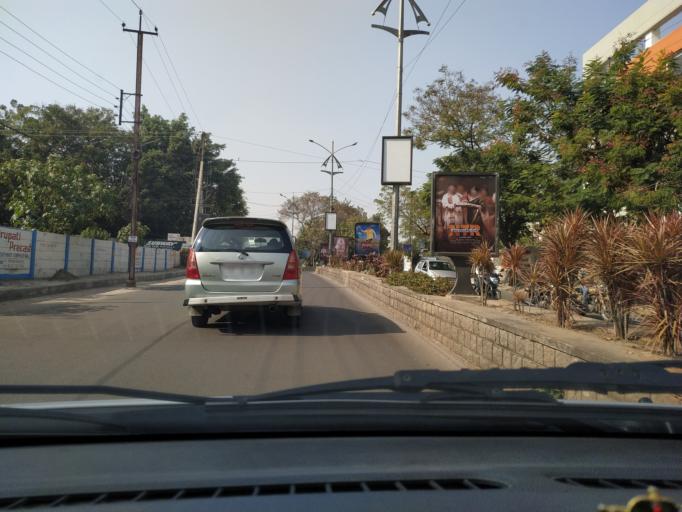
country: IN
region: Telangana
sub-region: Rangareddi
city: Kukatpalli
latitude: 17.4337
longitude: 78.4167
